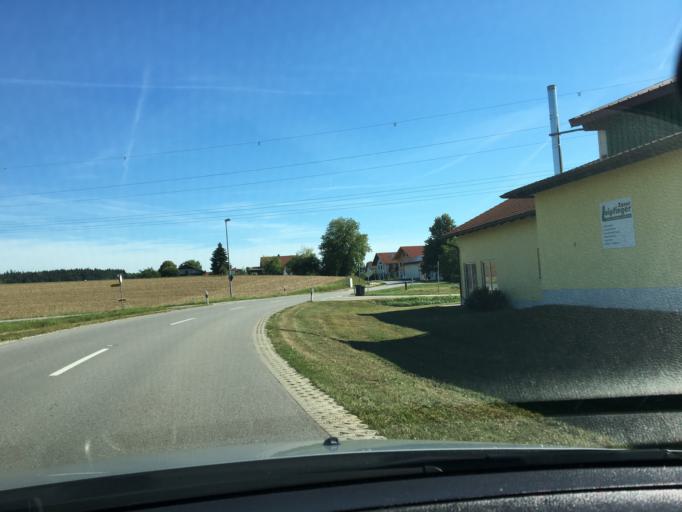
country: DE
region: Bavaria
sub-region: Lower Bavaria
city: Bodenkirchen
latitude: 48.3755
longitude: 12.3716
